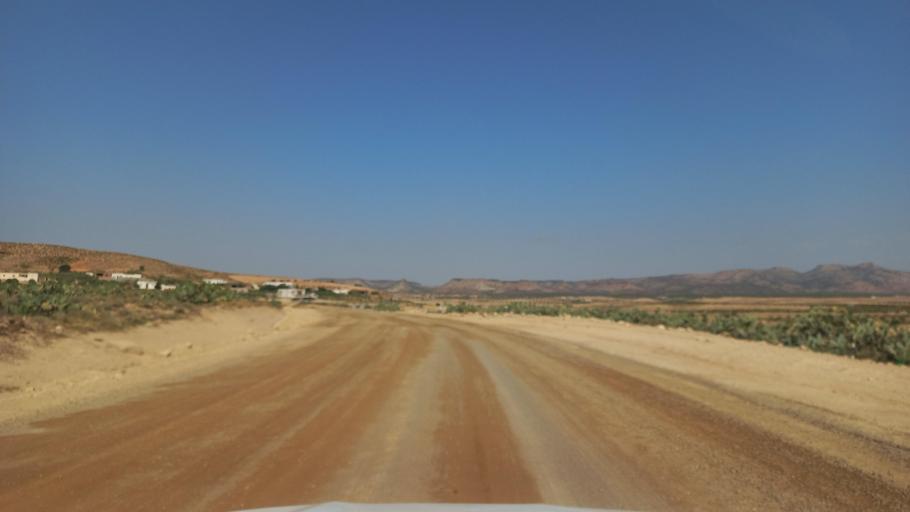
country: TN
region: Al Qasrayn
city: Sbiba
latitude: 35.3829
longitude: 9.0282
